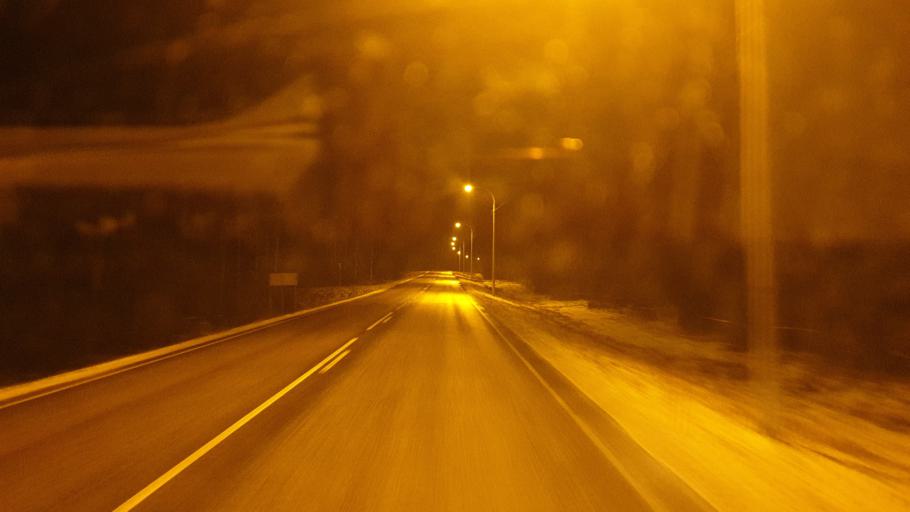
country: FI
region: Northern Savo
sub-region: Sisae-Savo
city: Suonenjoki
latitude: 62.6419
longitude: 27.2298
